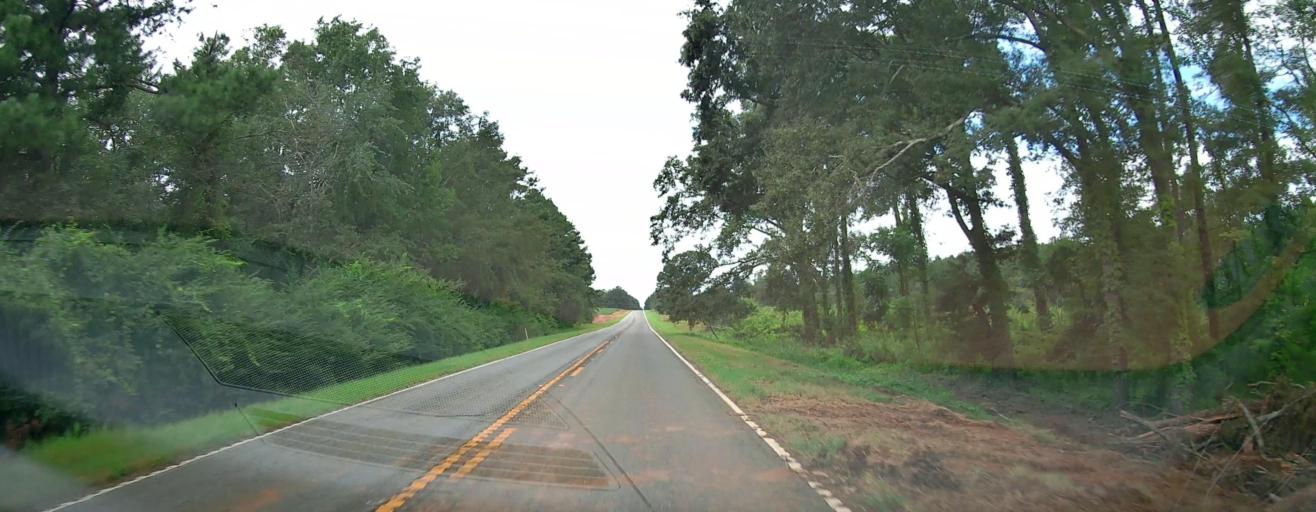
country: US
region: Georgia
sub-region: Dooly County
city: Unadilla
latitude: 32.2908
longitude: -83.8381
